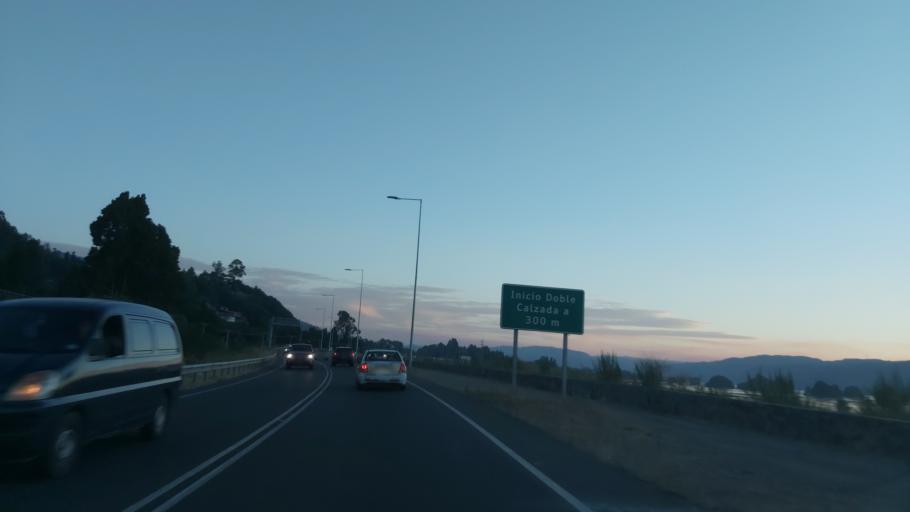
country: CL
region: Biobio
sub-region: Provincia de Concepcion
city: Chiguayante
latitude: -36.8880
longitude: -73.0380
